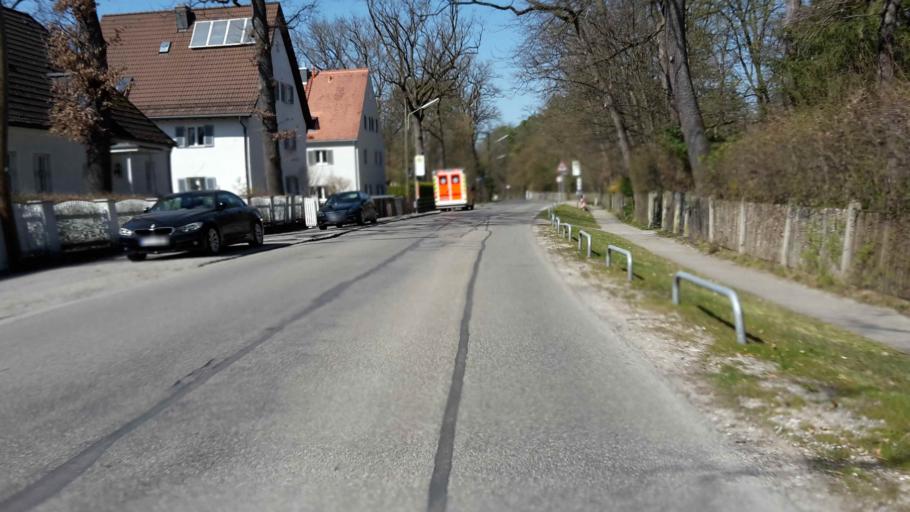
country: DE
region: Bavaria
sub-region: Upper Bavaria
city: Pasing
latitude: 48.1685
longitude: 11.4855
